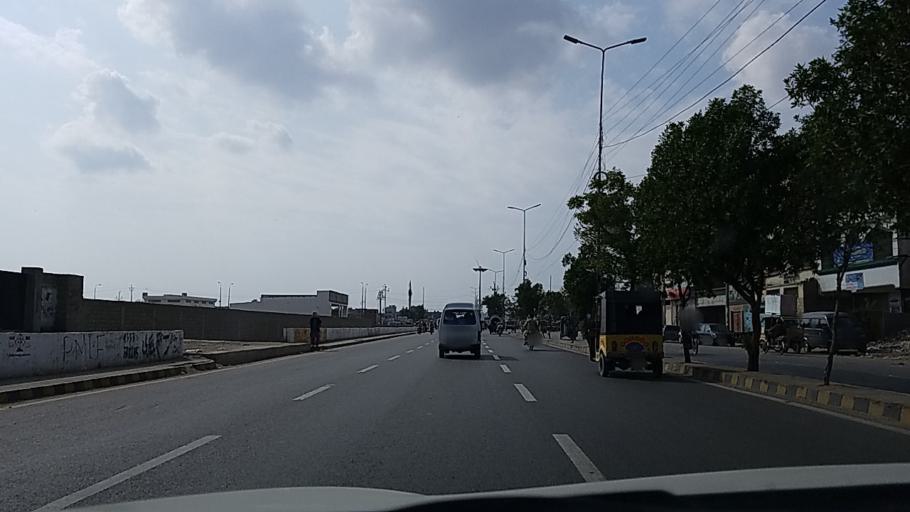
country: PK
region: Sindh
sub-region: Karachi District
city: Karachi
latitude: 24.8208
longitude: 67.1269
